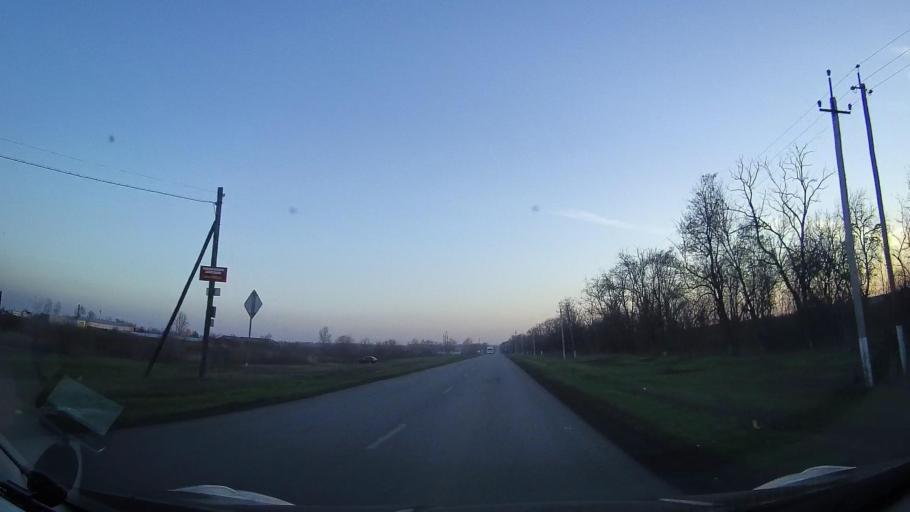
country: RU
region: Rostov
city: Zernograd
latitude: 47.0480
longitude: 40.3915
